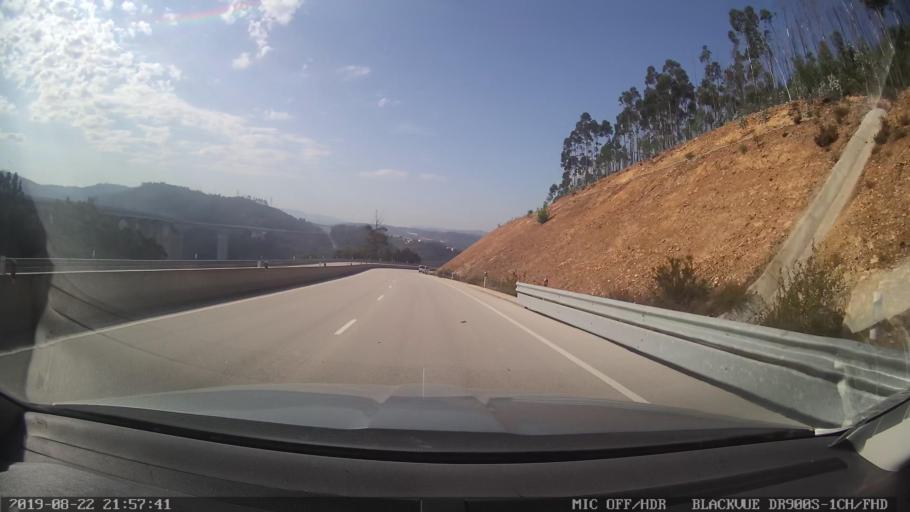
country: PT
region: Coimbra
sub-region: Coimbra
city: Coimbra
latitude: 40.1802
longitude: -8.3812
